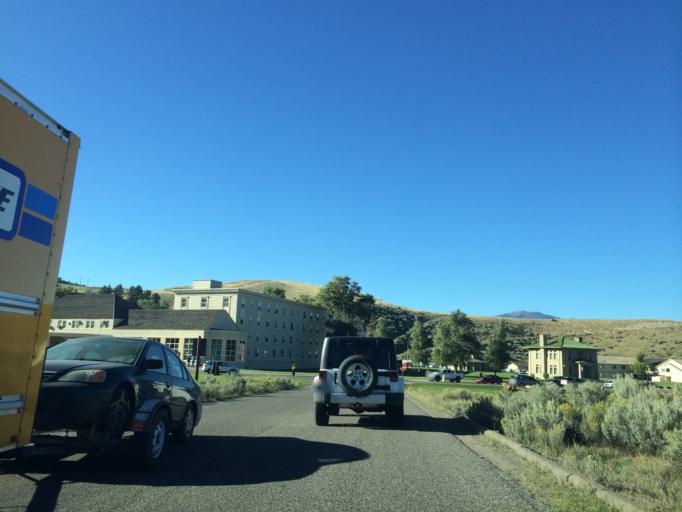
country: US
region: Montana
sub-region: Gallatin County
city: West Yellowstone
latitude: 44.9756
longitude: -110.7006
